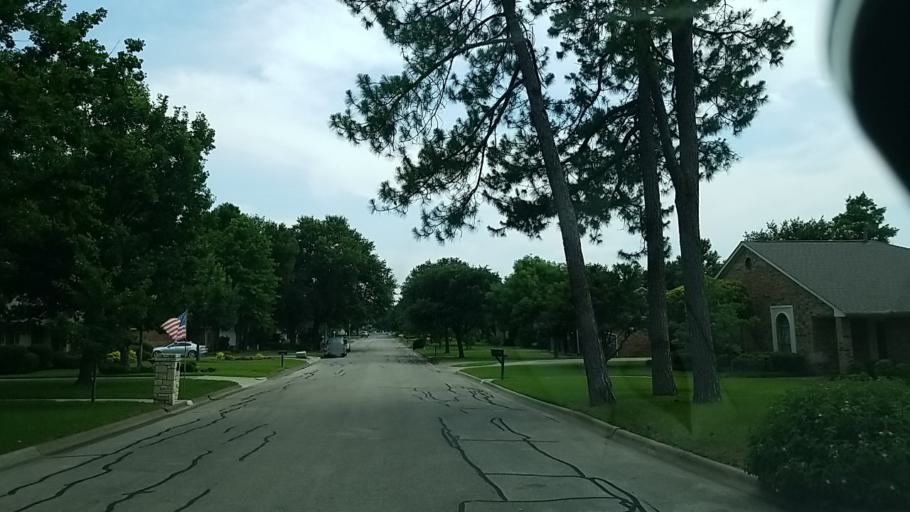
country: US
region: Texas
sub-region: Denton County
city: Denton
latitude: 33.1853
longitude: -97.1239
